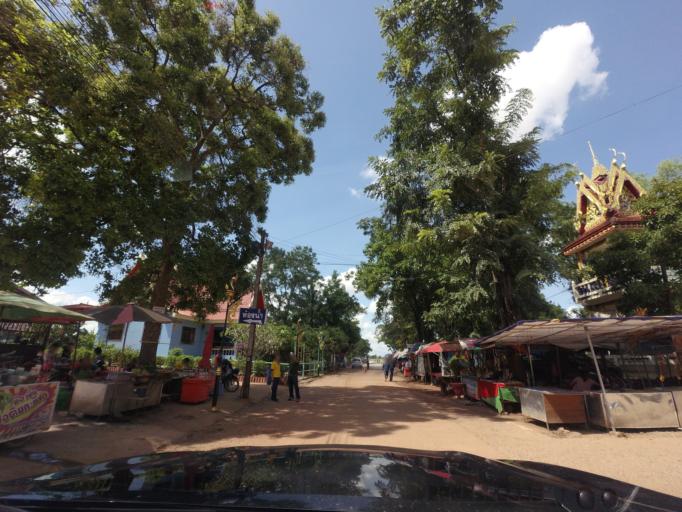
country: TH
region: Changwat Udon Thani
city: Ban Dung
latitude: 17.7432
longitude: 103.3585
